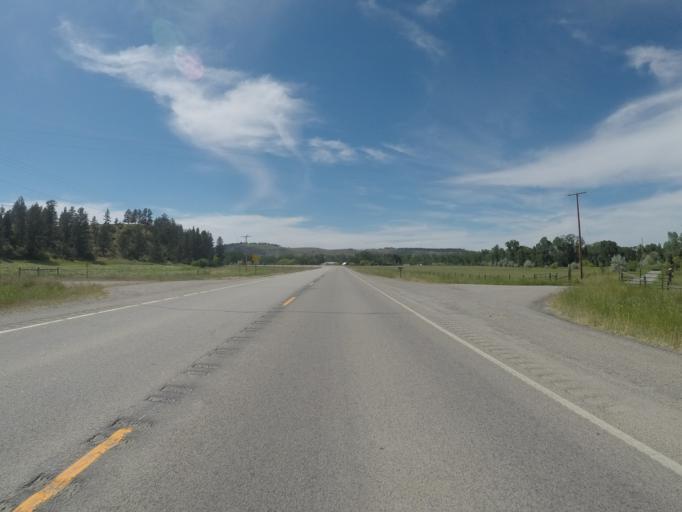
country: US
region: Montana
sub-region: Stillwater County
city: Columbus
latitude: 45.6307
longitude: -109.2690
